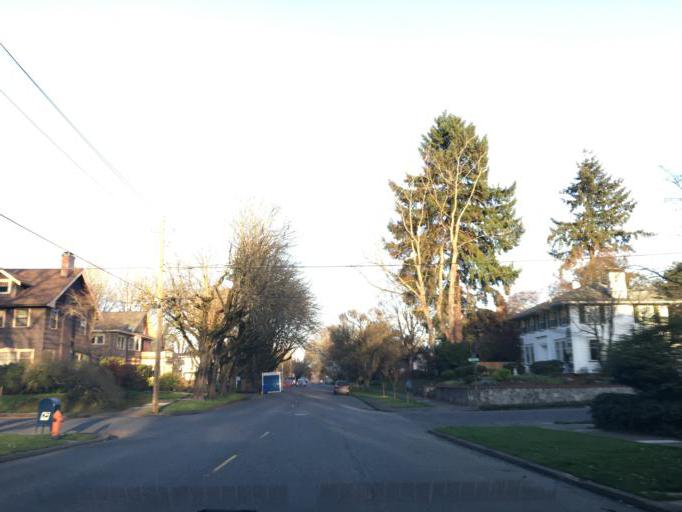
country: US
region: Oregon
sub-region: Multnomah County
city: Portland
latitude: 45.5421
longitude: -122.6438
